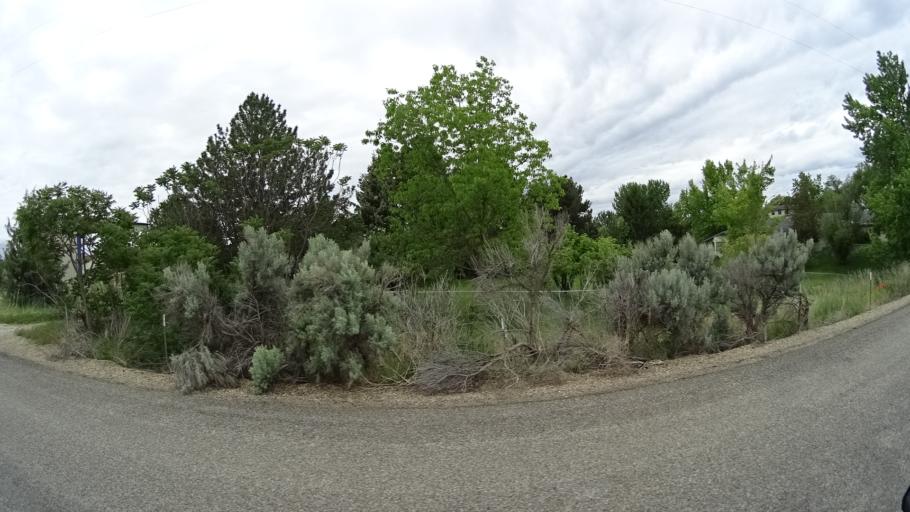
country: US
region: Idaho
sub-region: Ada County
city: Eagle
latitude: 43.7353
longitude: -116.3999
